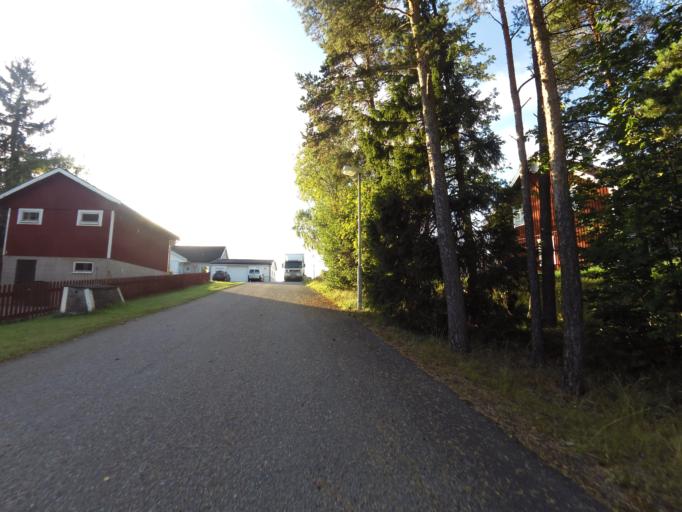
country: SE
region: Gaevleborg
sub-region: Gavle Kommun
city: Gavle
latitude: 60.7290
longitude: 17.1762
